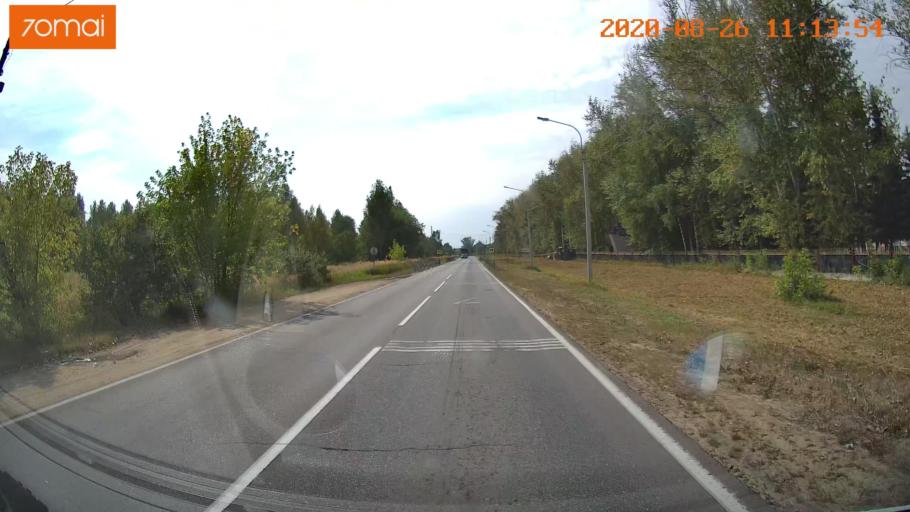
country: RU
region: Rjazan
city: Izhevskoye
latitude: 54.4526
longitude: 41.1184
